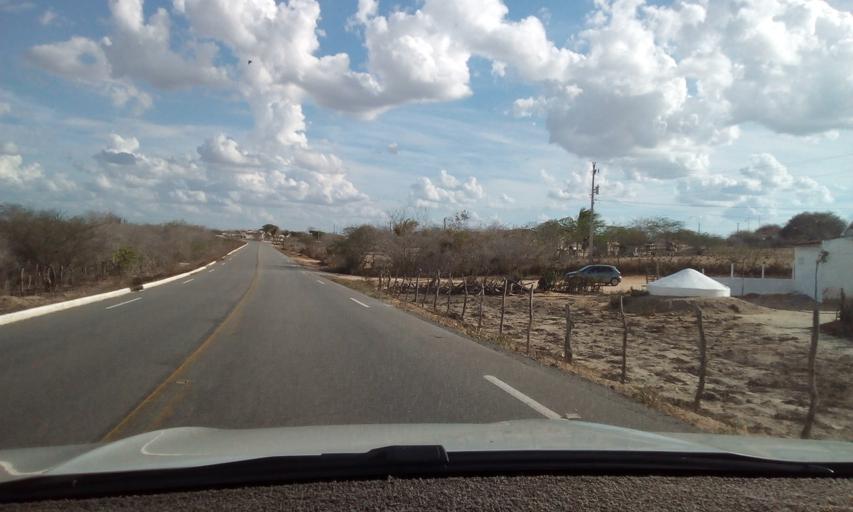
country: BR
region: Paraiba
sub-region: Soledade
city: Soledade
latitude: -6.8898
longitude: -36.3983
